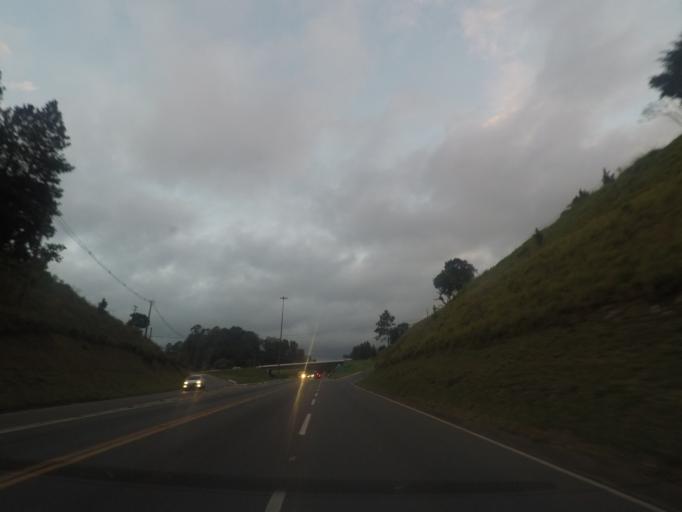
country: BR
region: Parana
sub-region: Almirante Tamandare
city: Almirante Tamandare
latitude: -25.3907
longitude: -49.3570
